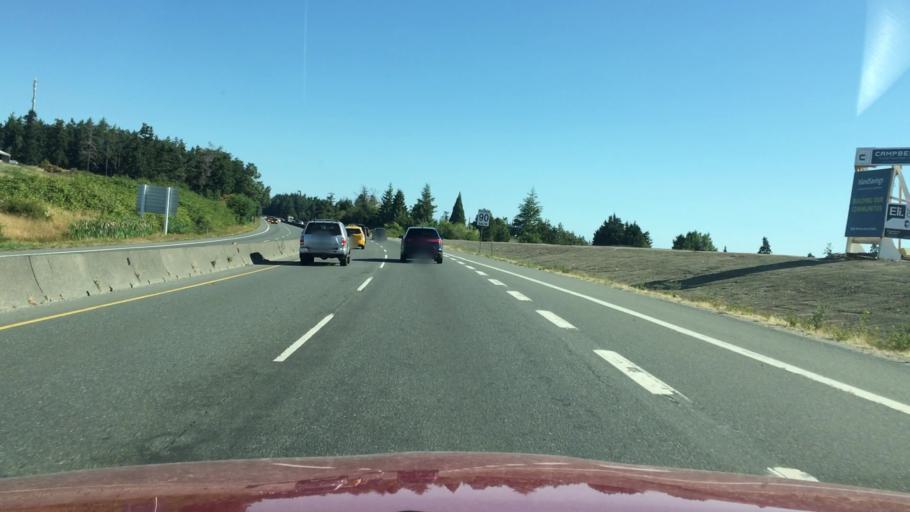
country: CA
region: British Columbia
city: North Saanich
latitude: 48.5968
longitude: -123.3969
